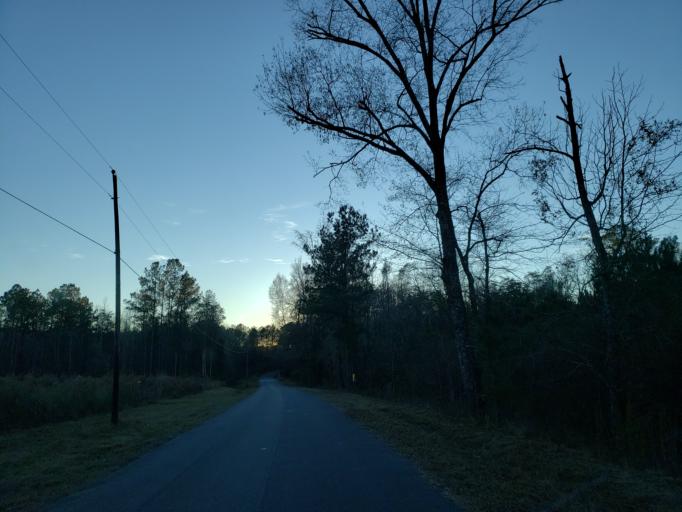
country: US
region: Mississippi
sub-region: Covington County
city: Collins
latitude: 31.5736
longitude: -89.4521
